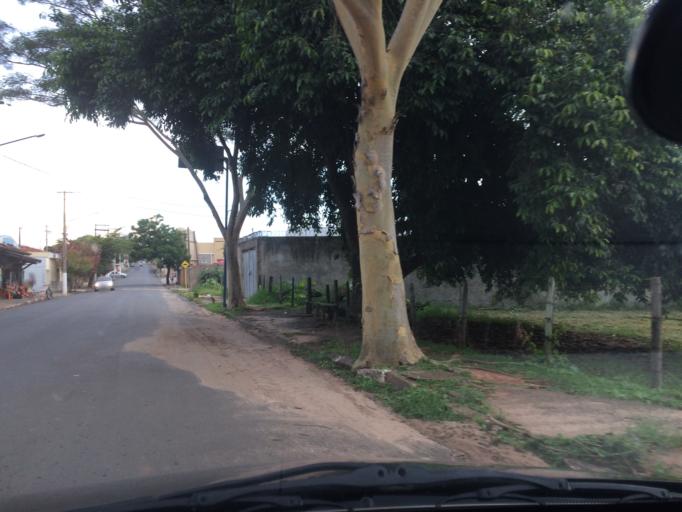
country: BR
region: Sao Paulo
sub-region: Casa Branca
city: Casa Branca
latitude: -21.7680
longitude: -47.0914
